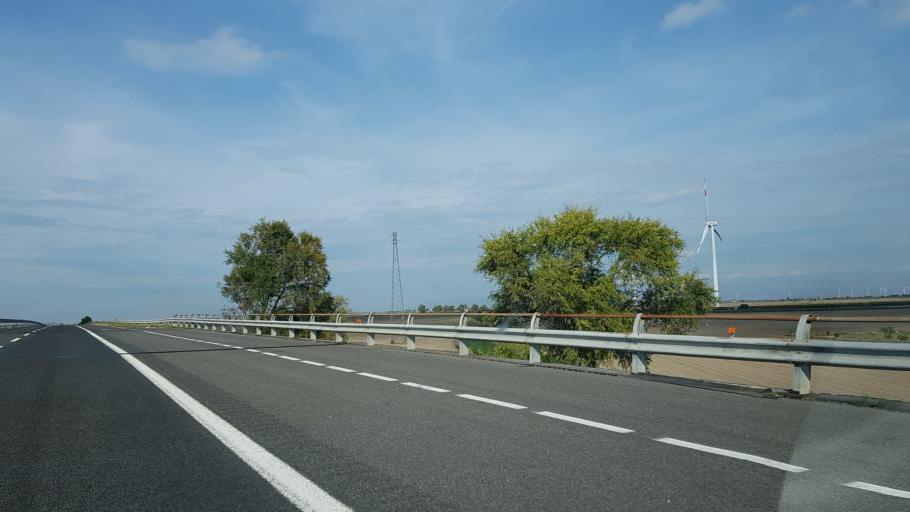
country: IT
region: Apulia
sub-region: Provincia di Foggia
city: Orta Nova
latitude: 41.3720
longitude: 15.7683
